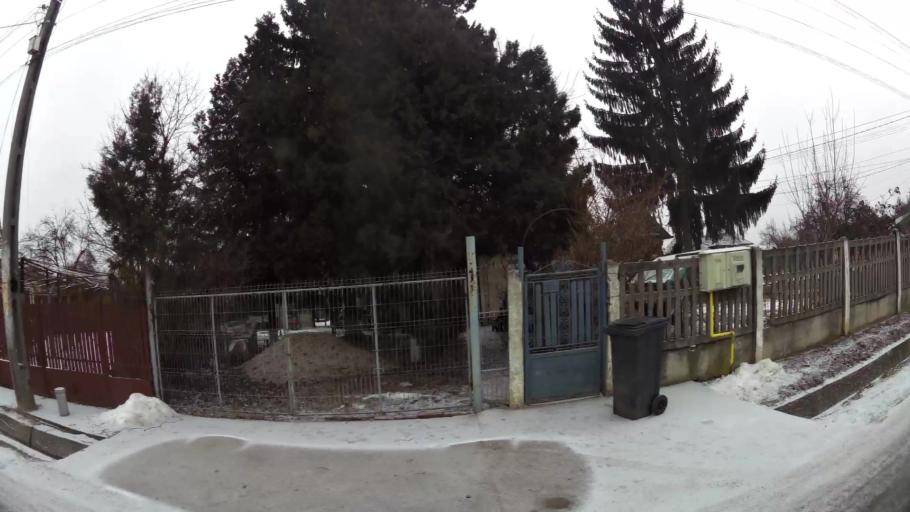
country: RO
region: Dambovita
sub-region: Municipiul Targoviste
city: Targoviste
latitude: 44.9409
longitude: 25.4752
